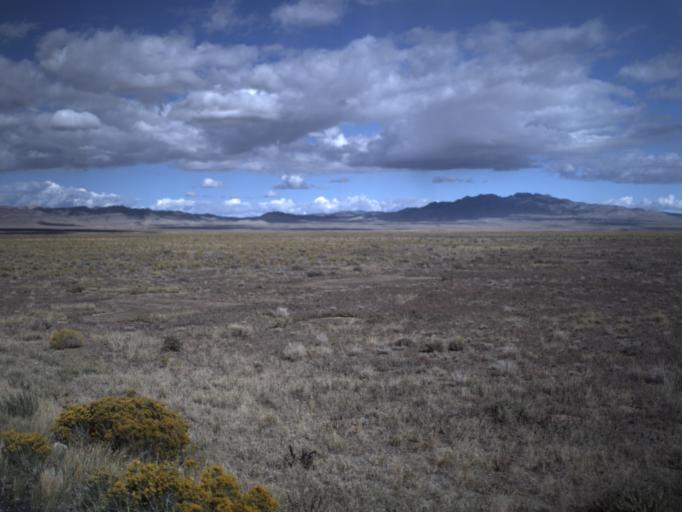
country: US
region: Utah
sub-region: Beaver County
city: Milford
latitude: 38.5326
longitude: -113.6826
